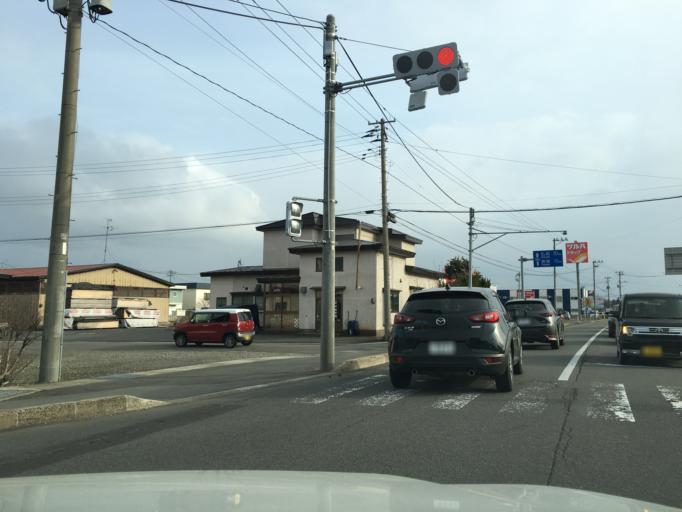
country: JP
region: Aomori
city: Namioka
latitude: 40.7216
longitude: 140.5889
